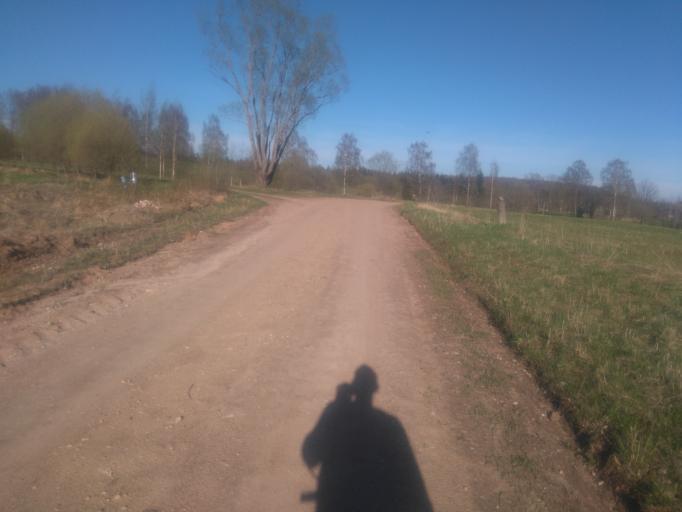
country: LV
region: Vecpiebalga
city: Vecpiebalga
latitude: 57.0254
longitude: 25.8583
